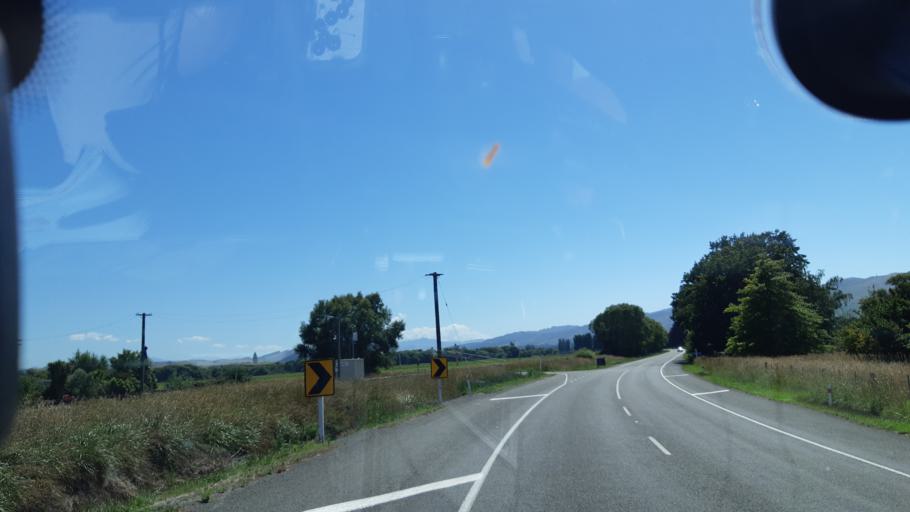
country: NZ
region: Canterbury
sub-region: Kaikoura District
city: Kaikoura
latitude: -42.7388
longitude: 173.2667
